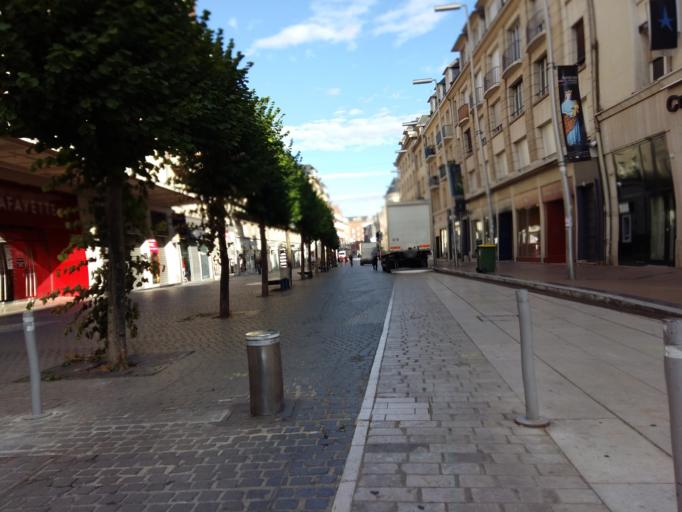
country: FR
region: Picardie
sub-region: Departement de la Somme
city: Amiens
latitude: 49.8927
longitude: 2.2989
